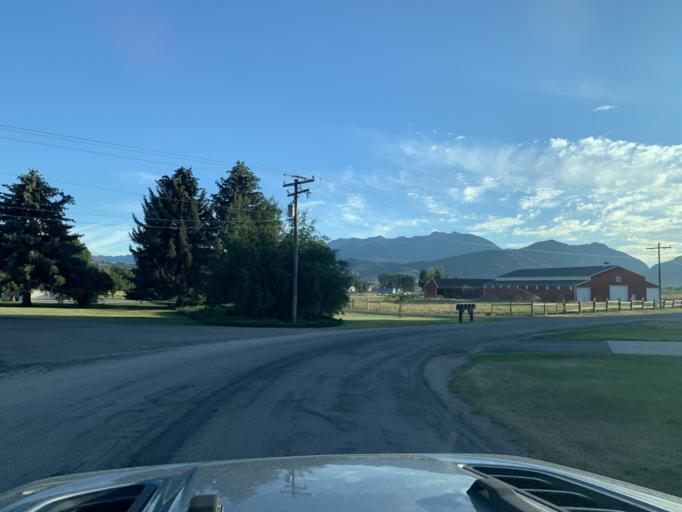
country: US
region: Utah
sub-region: Weber County
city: Wolf Creek
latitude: 41.2828
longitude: -111.7586
